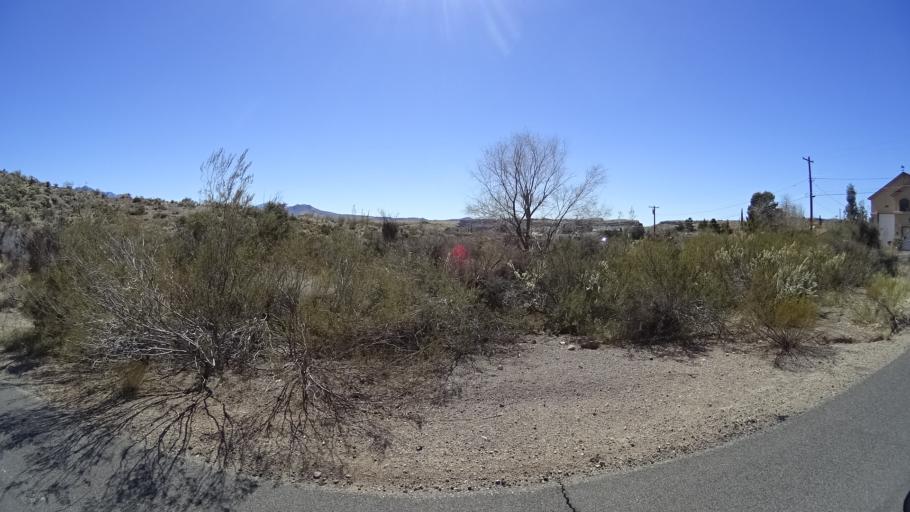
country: US
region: Arizona
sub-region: Mohave County
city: Kingman
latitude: 35.1992
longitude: -114.0603
